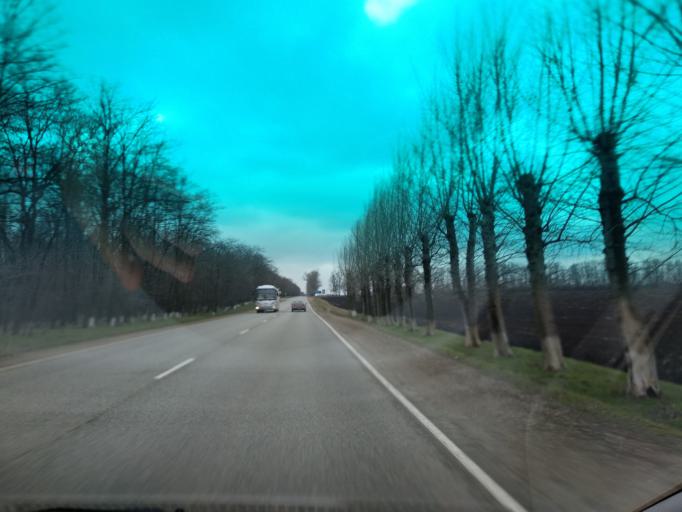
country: RU
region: Krasnodarskiy
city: Novorozhdestvenskaya
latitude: 45.7820
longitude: 39.9678
